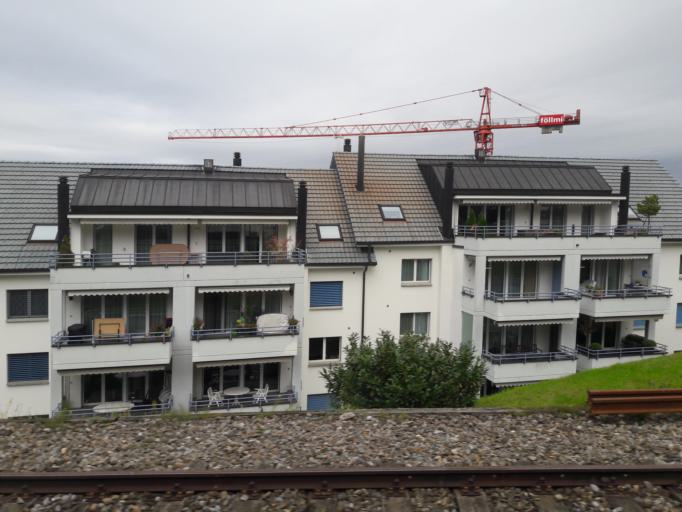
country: CH
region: Schwyz
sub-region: Bezirk Hoefe
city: Schindellegi
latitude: 47.1770
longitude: 8.7085
